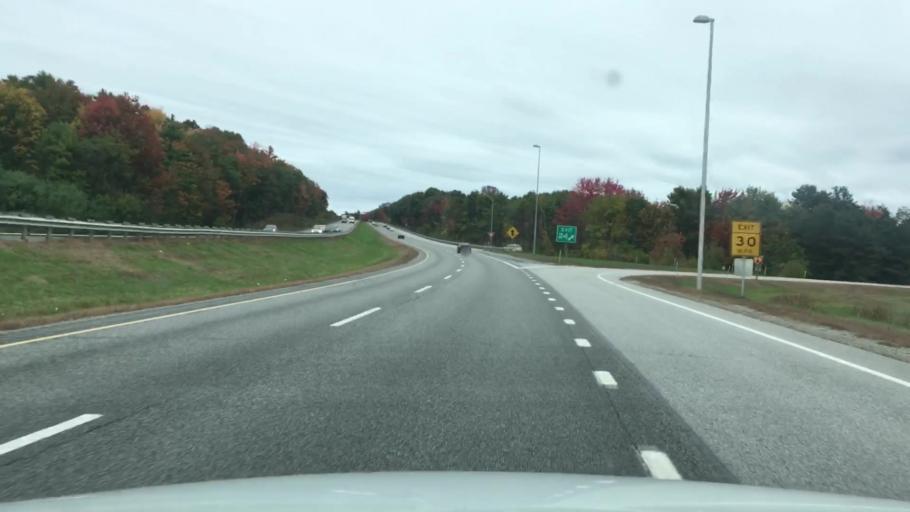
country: US
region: Maine
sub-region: Cumberland County
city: Freeport
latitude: 43.8775
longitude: -70.0856
